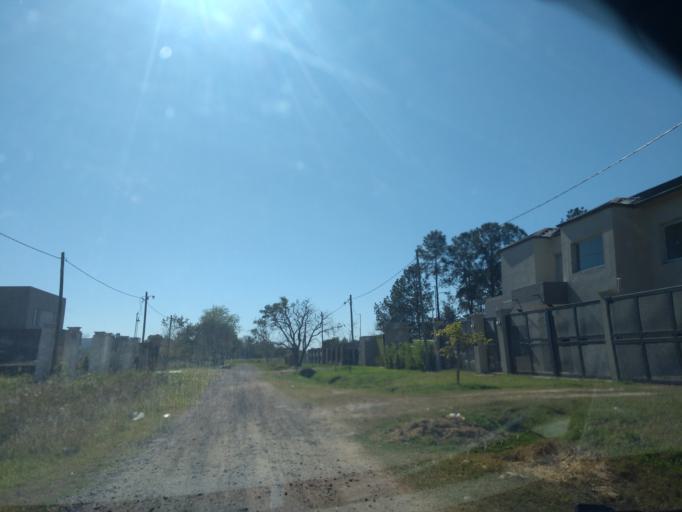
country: AR
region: Chaco
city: Resistencia
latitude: -27.4236
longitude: -58.9450
